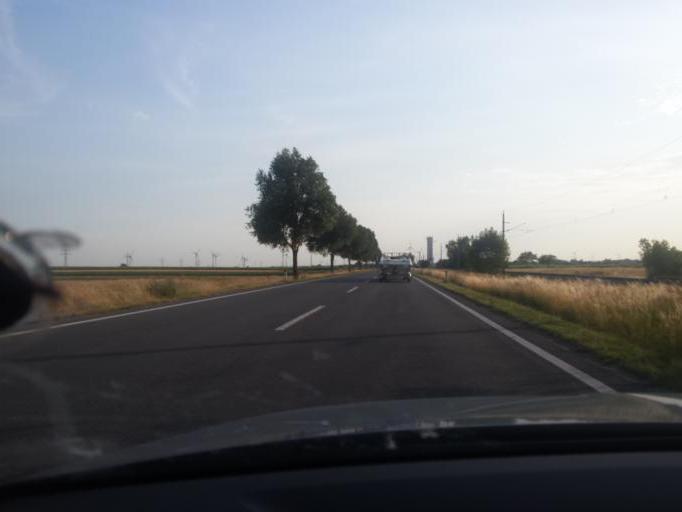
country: AT
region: Lower Austria
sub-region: Politischer Bezirk Bruck an der Leitha
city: Bad Deutsch-Altenburg
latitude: 48.1135
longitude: 16.8839
